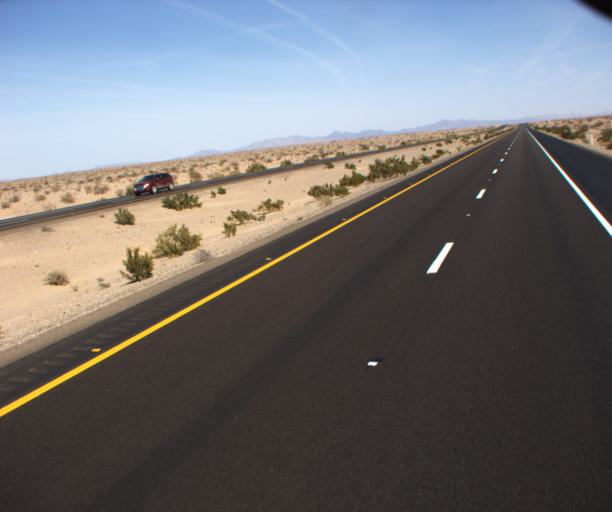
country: US
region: Arizona
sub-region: Yuma County
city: Somerton
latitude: 32.4951
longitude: -114.6248
